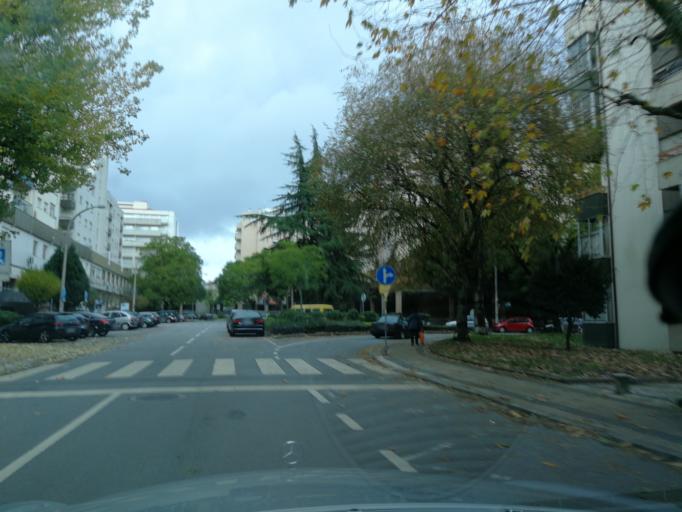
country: PT
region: Braga
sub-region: Braga
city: Braga
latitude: 41.5484
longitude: -8.4112
